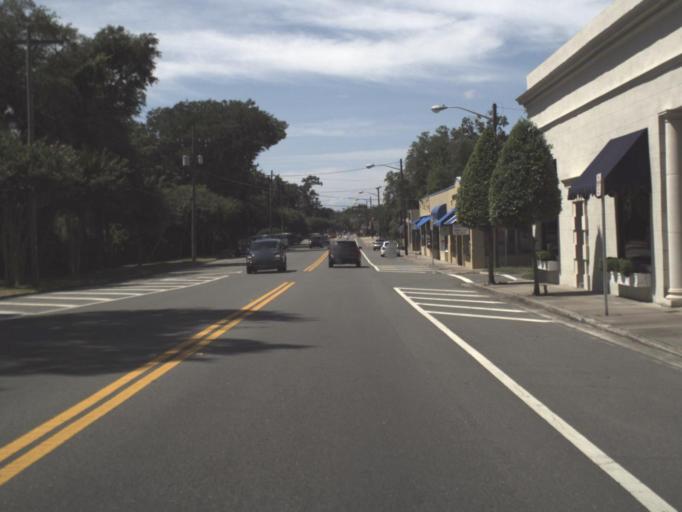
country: US
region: Florida
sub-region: Duval County
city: Jacksonville
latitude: 30.2880
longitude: -81.7135
